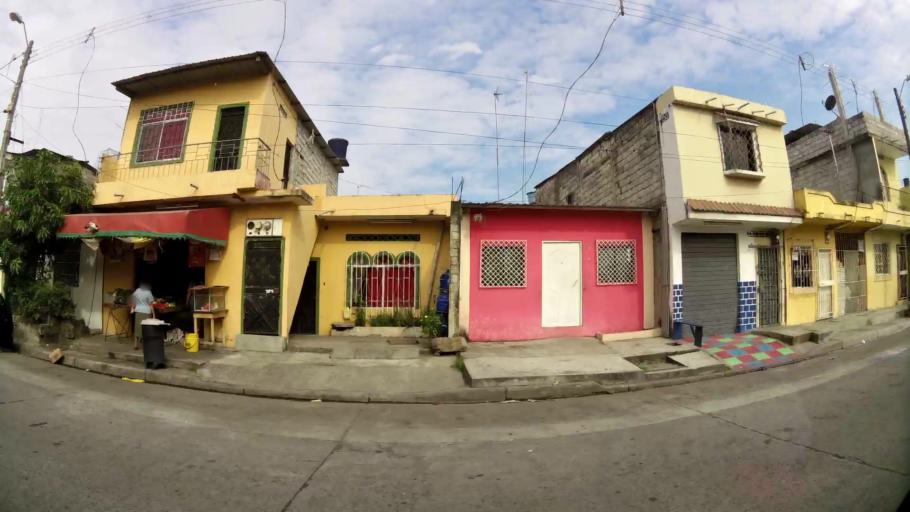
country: EC
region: Guayas
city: Guayaquil
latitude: -2.2490
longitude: -79.8877
